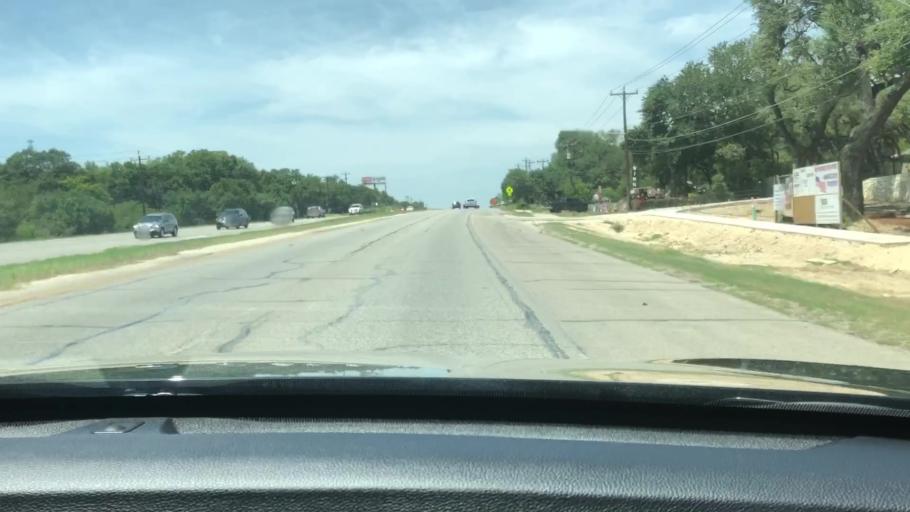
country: US
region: Texas
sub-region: Bexar County
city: Helotes
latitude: 29.5445
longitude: -98.6582
